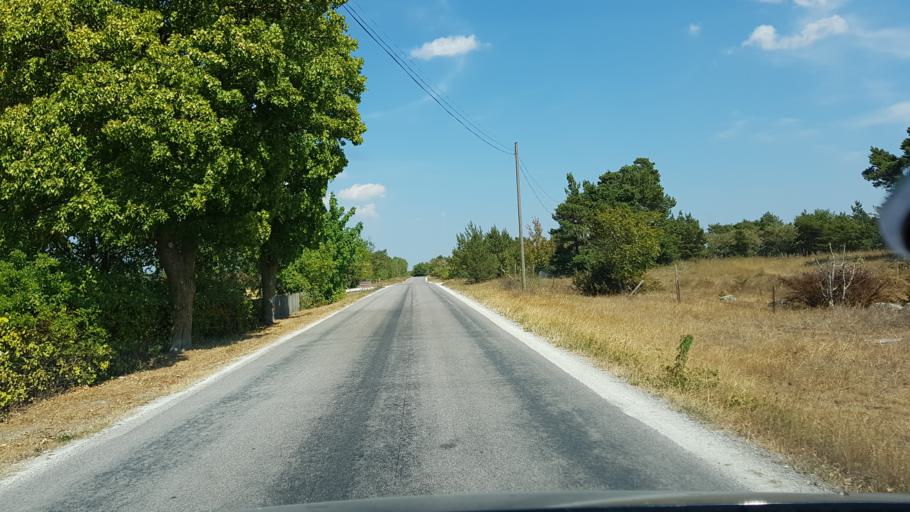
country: SE
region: Gotland
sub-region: Gotland
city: Visby
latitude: 57.6540
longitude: 18.3578
